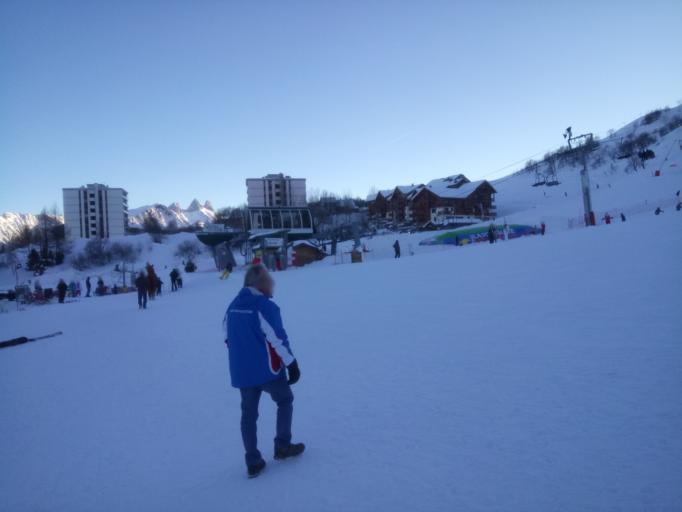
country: FR
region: Rhone-Alpes
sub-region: Departement de la Savoie
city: Saint-Jean-de-Maurienne
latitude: 45.2551
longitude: 6.2568
